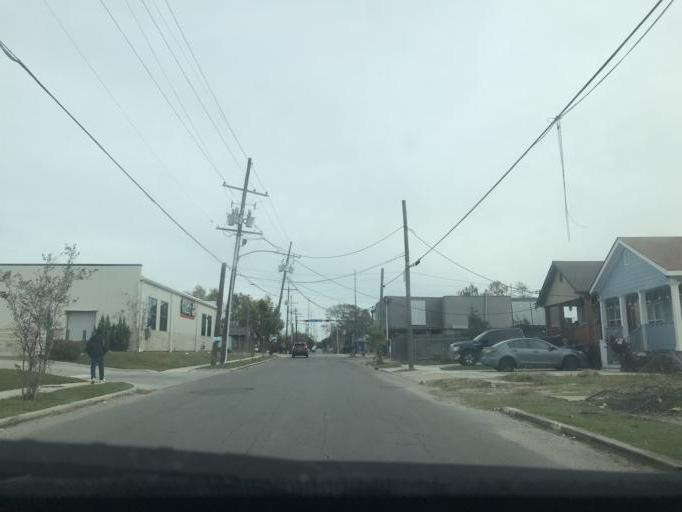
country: US
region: Louisiana
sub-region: Orleans Parish
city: New Orleans
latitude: 29.9583
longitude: -90.1115
